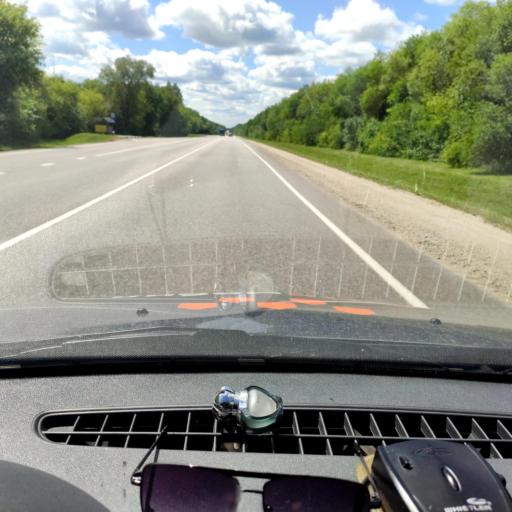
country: RU
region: Lipetsk
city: Borinskoye
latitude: 52.3939
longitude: 39.2316
